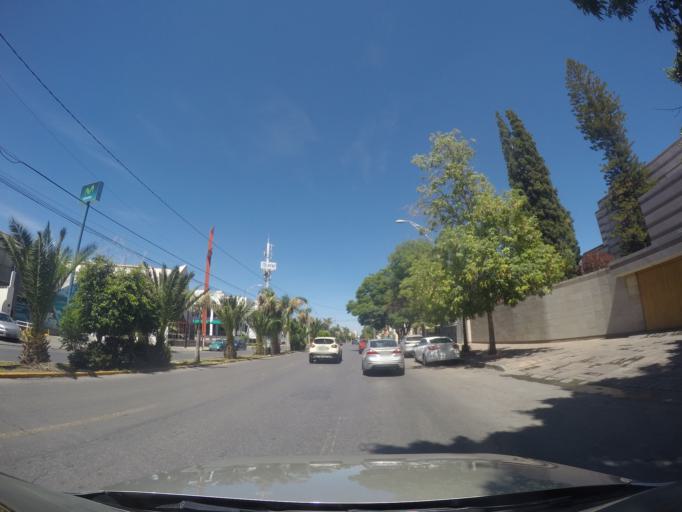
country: MX
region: San Luis Potosi
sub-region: San Luis Potosi
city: San Luis Potosi
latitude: 22.1491
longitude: -101.0061
